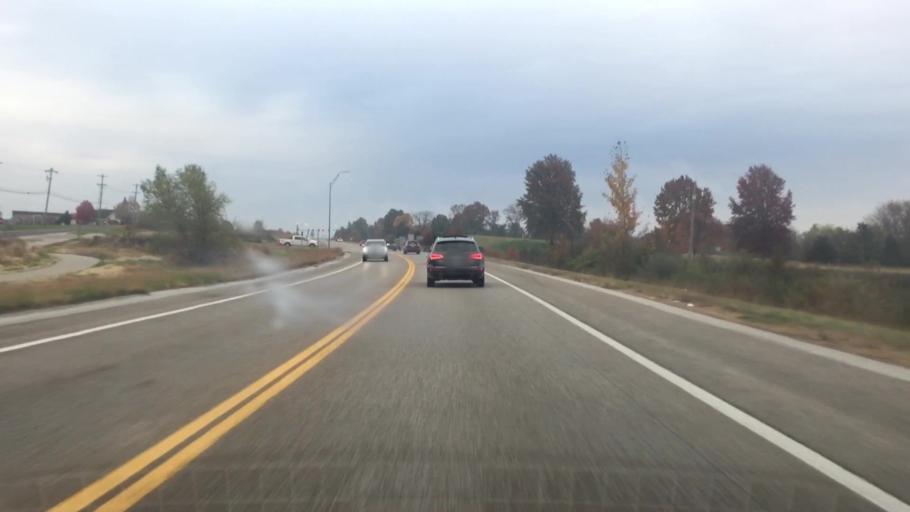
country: US
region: Missouri
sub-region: Boone County
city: Columbia
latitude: 38.8943
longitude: -92.3353
